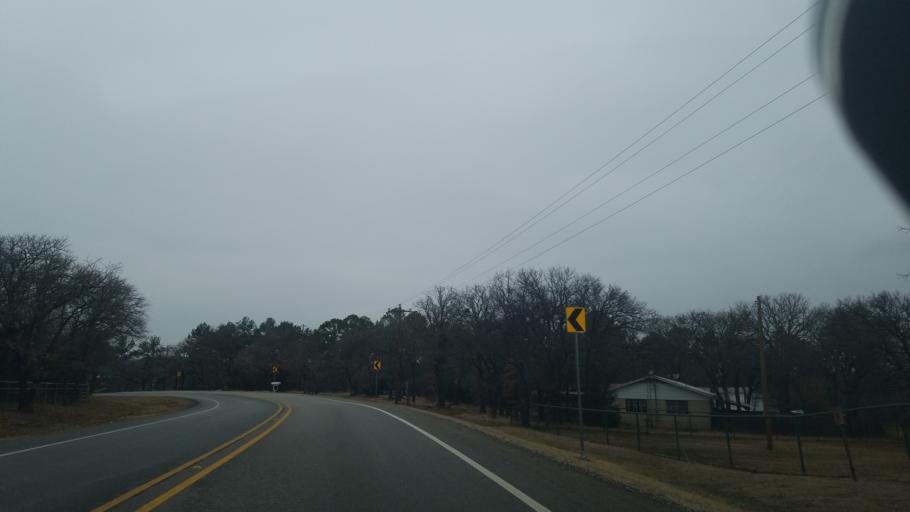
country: US
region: Texas
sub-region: Denton County
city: Argyle
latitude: 33.1317
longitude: -97.1451
